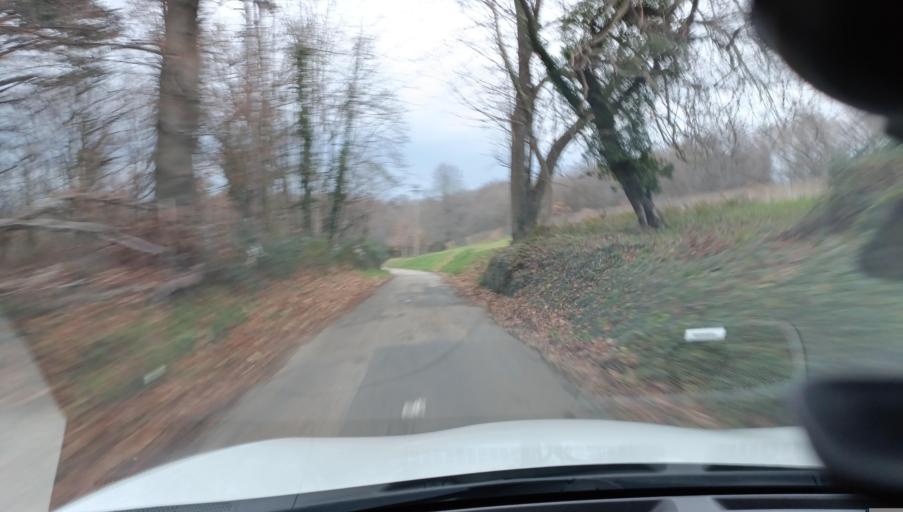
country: FR
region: Rhone-Alpes
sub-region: Departement de l'Isere
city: Chasse-sur-Rhone
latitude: 45.5743
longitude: 4.8230
